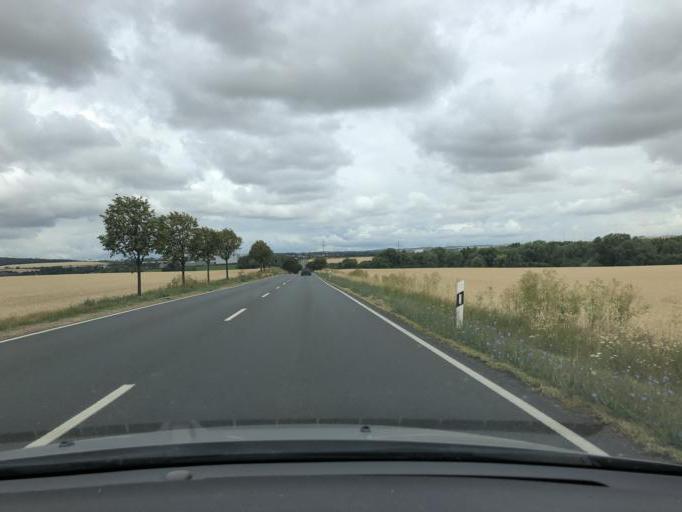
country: DE
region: Saxony-Anhalt
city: Erdeborn
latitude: 51.5003
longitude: 11.6201
